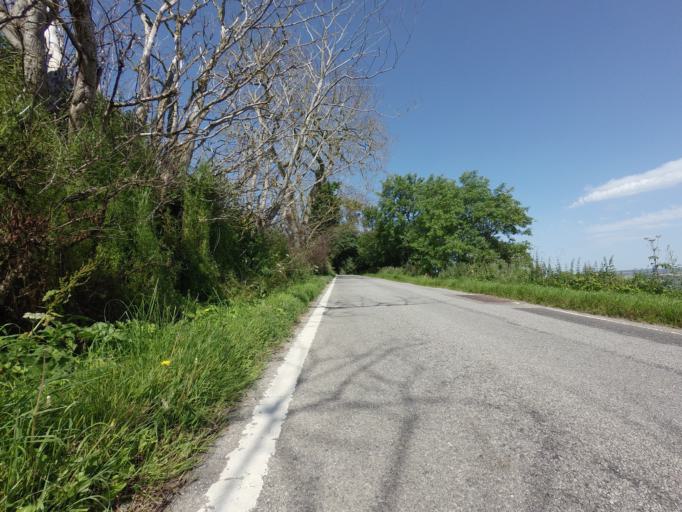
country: GB
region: Scotland
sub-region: Highland
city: Dingwall
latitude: 57.6160
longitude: -4.4073
